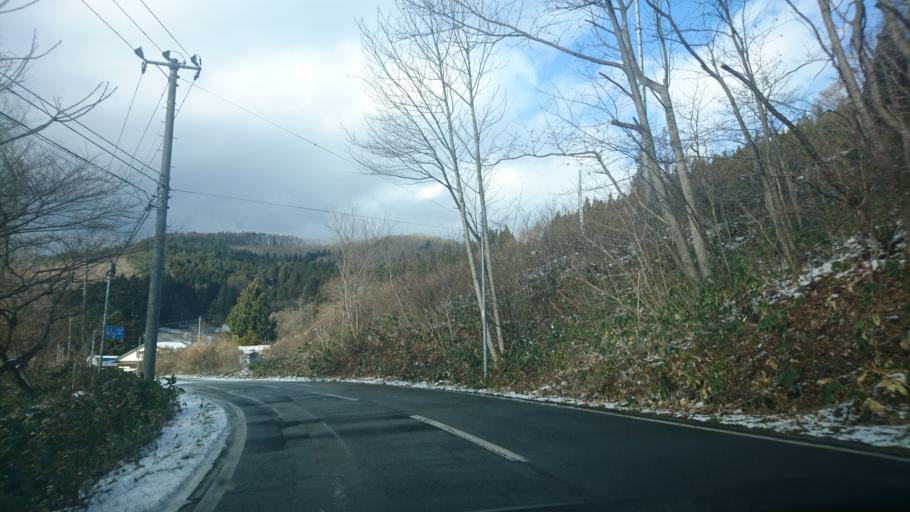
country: JP
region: Iwate
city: Tono
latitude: 39.1675
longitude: 141.3654
